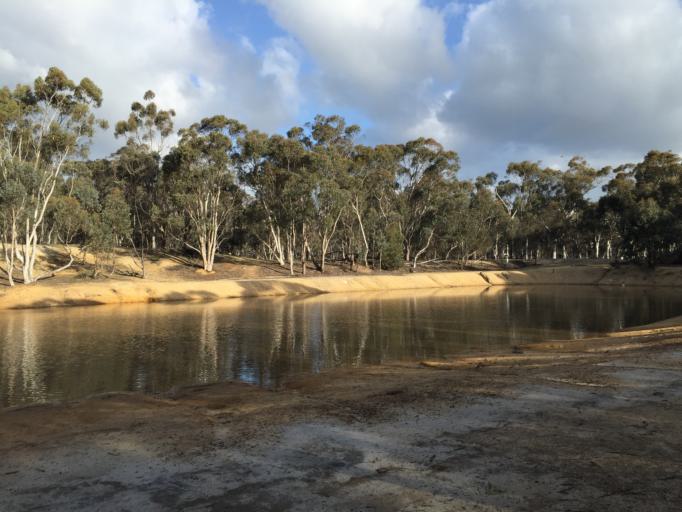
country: AU
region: Western Australia
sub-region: Narrogin
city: Narrogin
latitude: -32.7851
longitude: 116.9675
